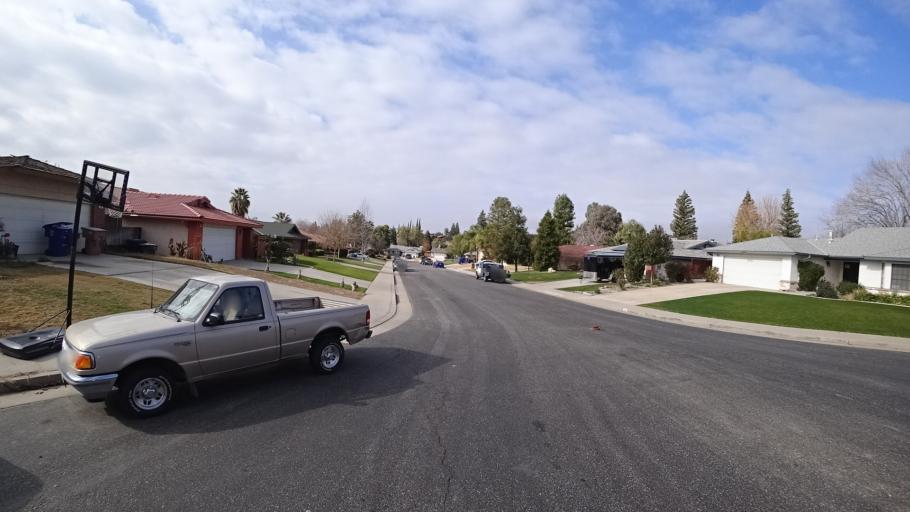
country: US
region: California
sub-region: Kern County
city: Bakersfield
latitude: 35.3886
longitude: -118.9264
